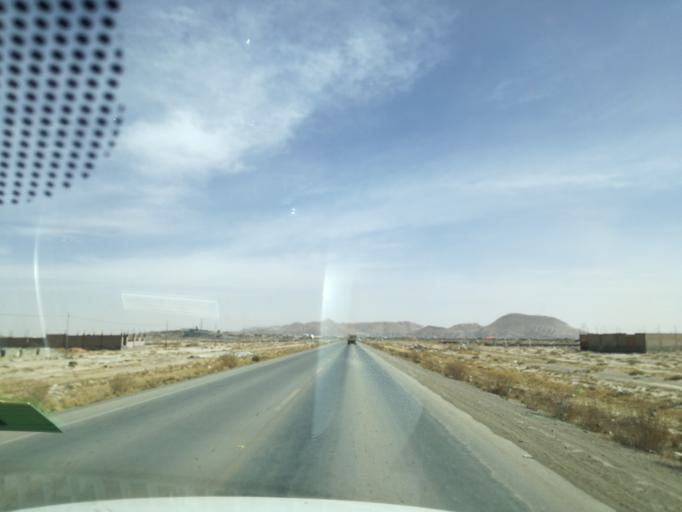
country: BO
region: Oruro
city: Oruro
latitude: -17.9107
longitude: -67.0638
